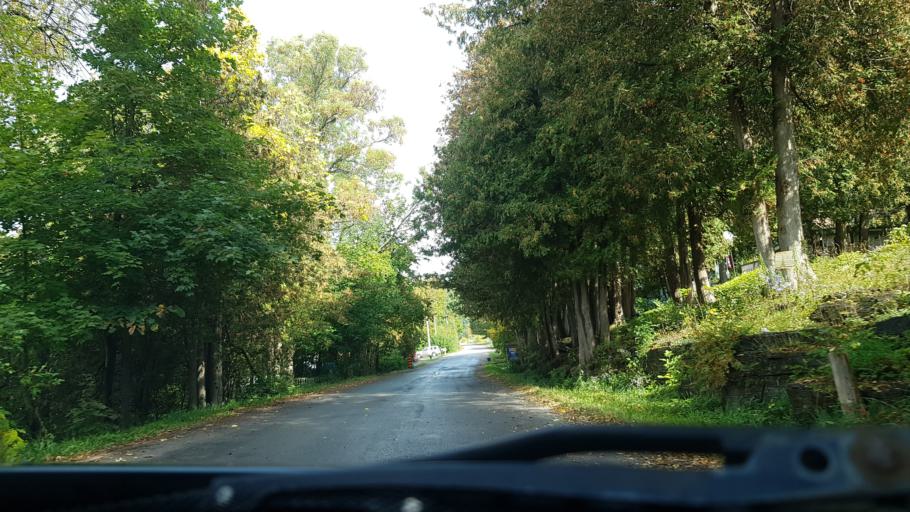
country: CA
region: Ontario
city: Orillia
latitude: 44.6657
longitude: -79.0974
